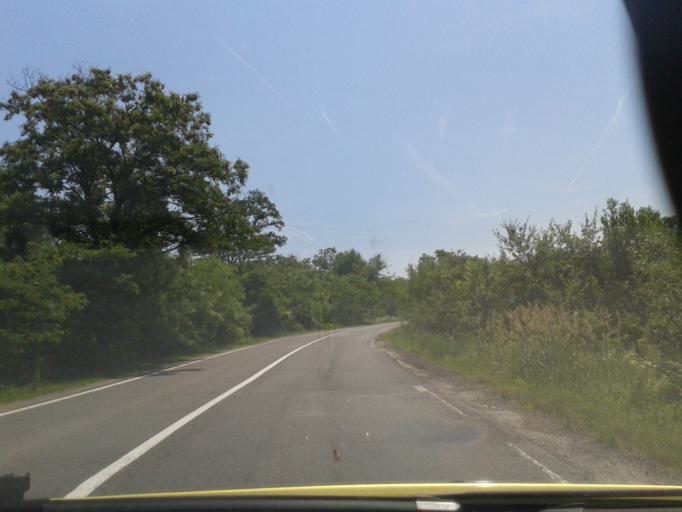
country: RO
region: Timis
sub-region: Comuna Curtea
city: Curtea
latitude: 45.8493
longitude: 22.3200
